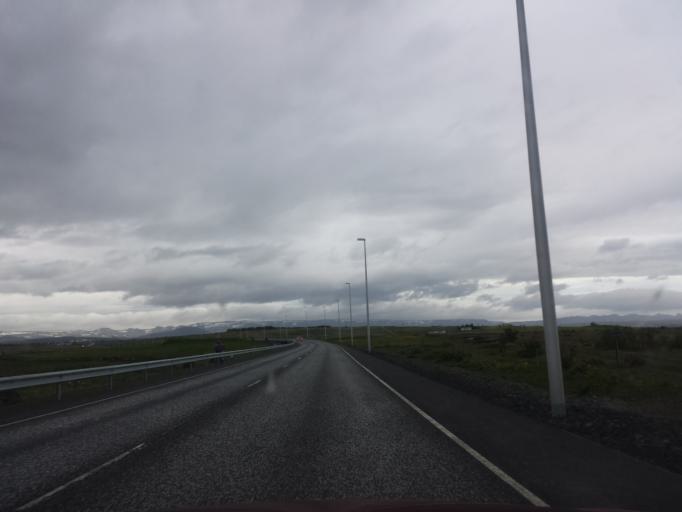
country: IS
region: Capital Region
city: Alftanes
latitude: 64.0998
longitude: -22.0074
